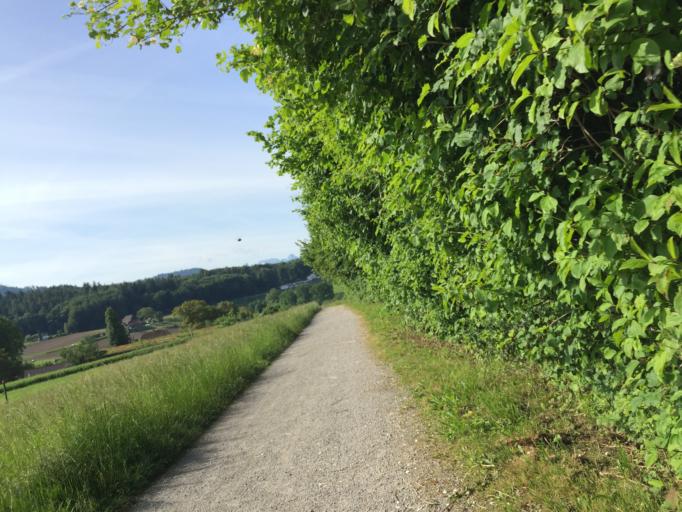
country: CH
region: Bern
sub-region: Bern-Mittelland District
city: Koniz
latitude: 46.9221
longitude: 7.4015
